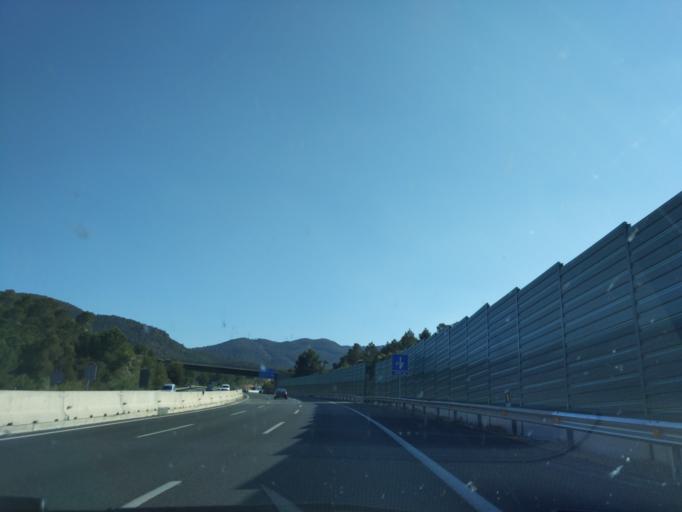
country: ES
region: Murcia
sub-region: Murcia
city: Murcia
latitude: 37.9267
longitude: -1.1570
